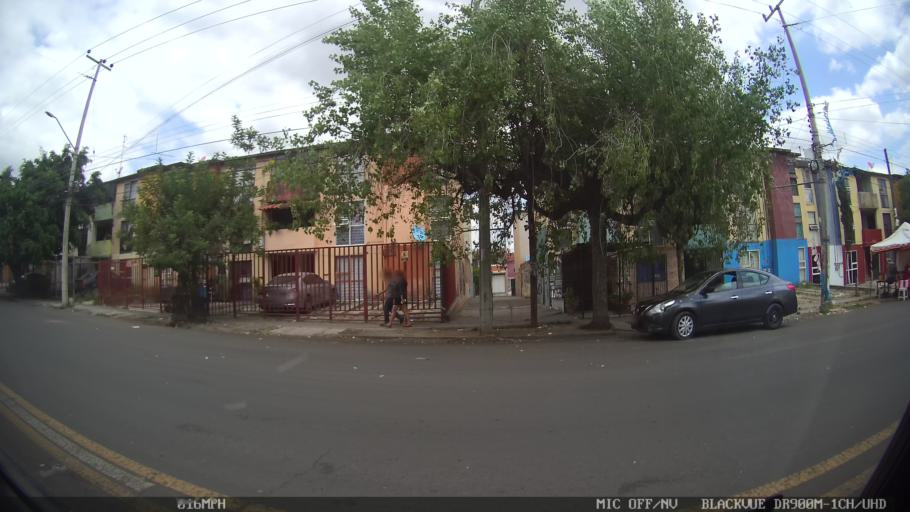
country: MX
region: Jalisco
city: Tonala
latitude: 20.6332
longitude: -103.2616
